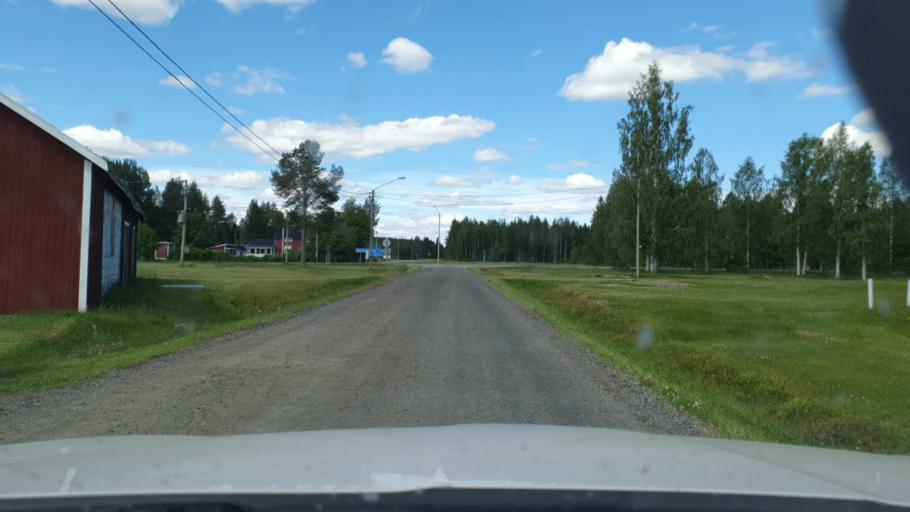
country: SE
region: Vaesterbotten
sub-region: Skelleftea Kommun
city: Backa
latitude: 65.1847
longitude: 21.0632
